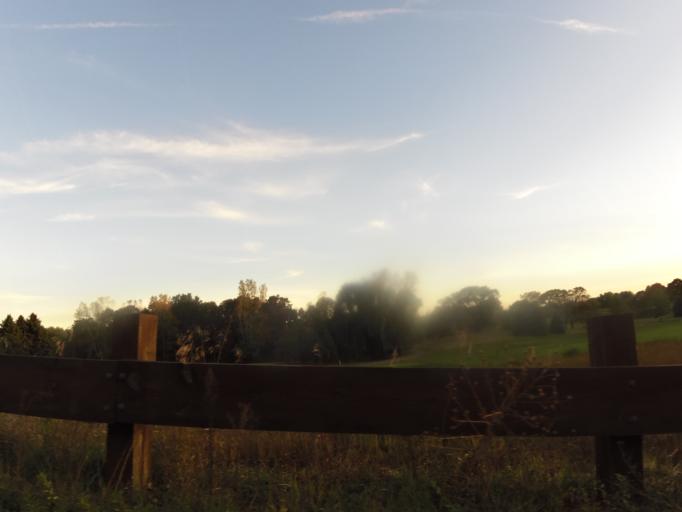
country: US
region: Minnesota
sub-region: Washington County
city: Lake Elmo
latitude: 44.9760
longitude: -92.8747
